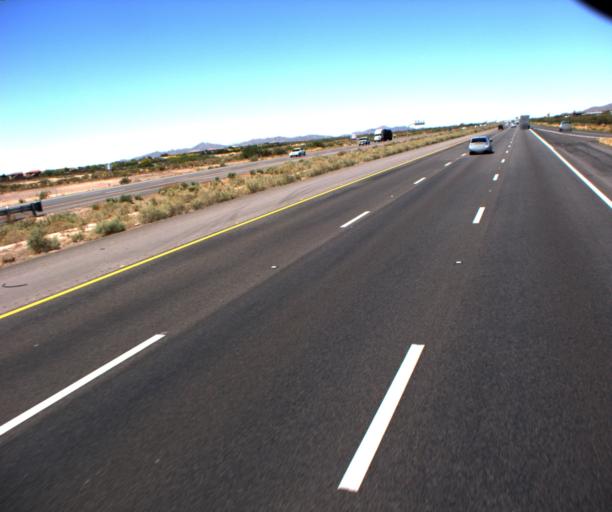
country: US
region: Arizona
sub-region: Pinal County
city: Casa Grande
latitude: 32.9401
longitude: -111.7021
